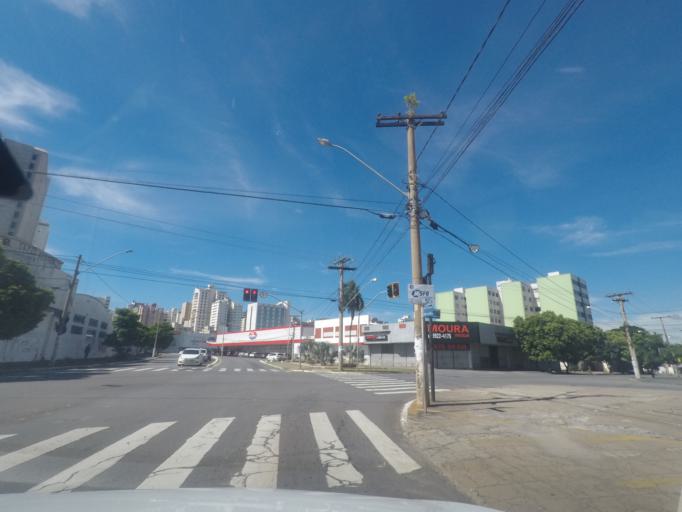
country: BR
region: Goias
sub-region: Goiania
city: Goiania
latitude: -16.6757
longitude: -49.2656
